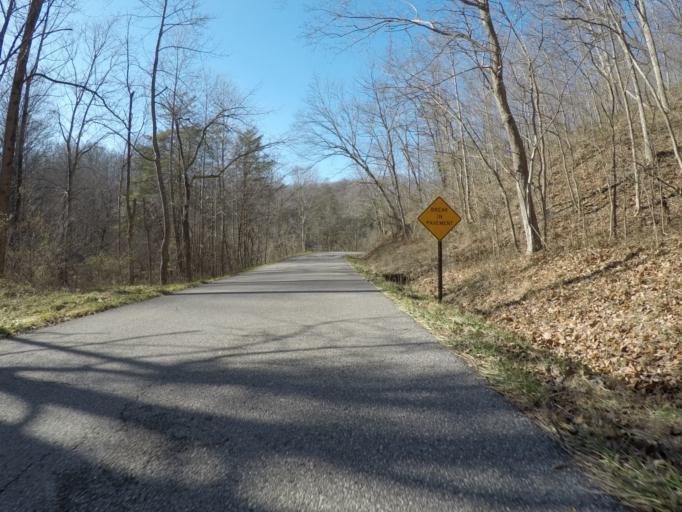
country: US
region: Kentucky
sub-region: Boyd County
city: Catlettsburg
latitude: 38.4035
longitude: -82.6339
